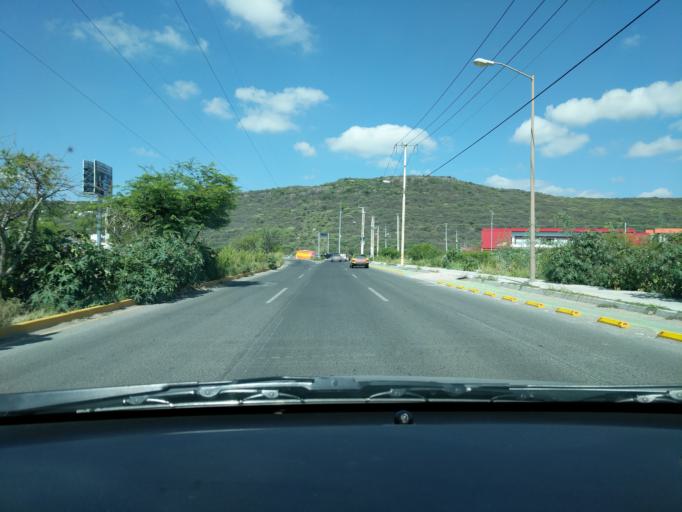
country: MX
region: Queretaro
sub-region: Queretaro
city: Patria Nueva
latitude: 20.6397
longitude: -100.4988
